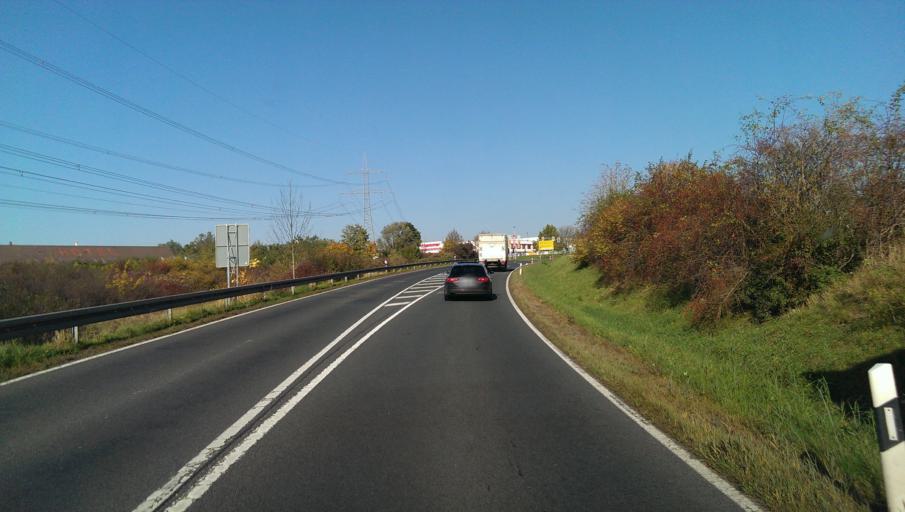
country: DE
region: Saxony
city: Ostrau
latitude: 51.2027
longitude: 13.1536
